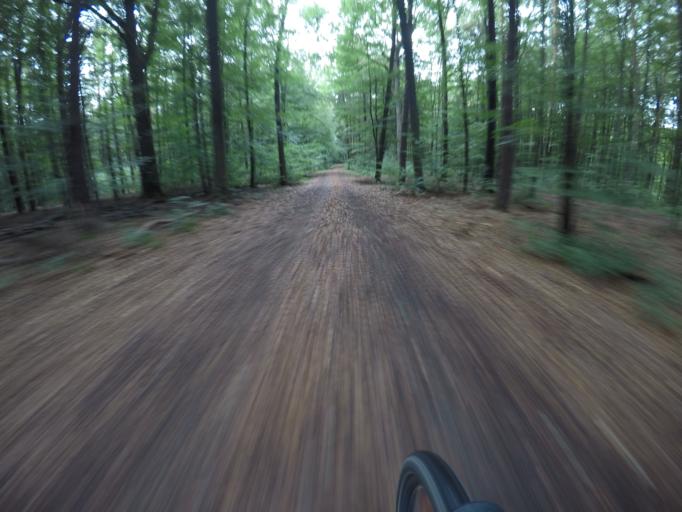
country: DE
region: Baden-Wuerttemberg
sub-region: Regierungsbezirk Stuttgart
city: Steinenbronn
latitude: 48.7256
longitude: 9.0840
